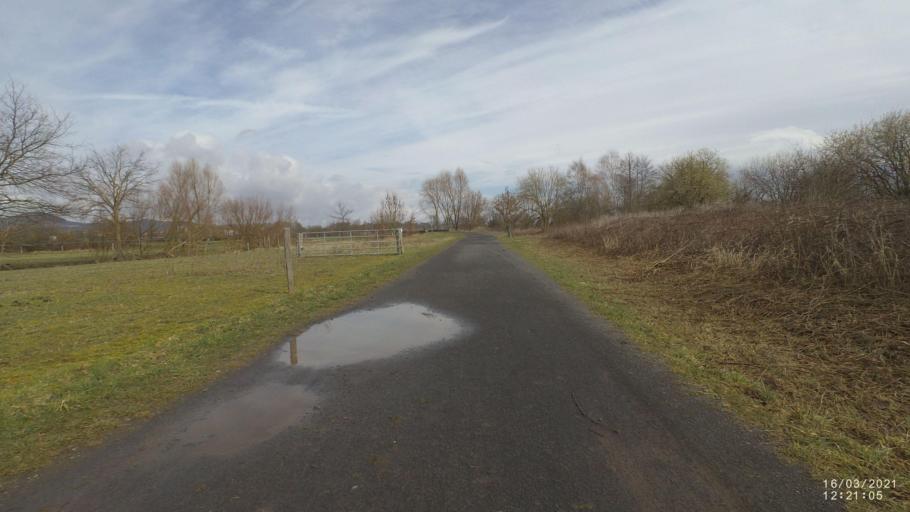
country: DE
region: Rheinland-Pfalz
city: Mendig
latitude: 50.3588
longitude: 7.2938
